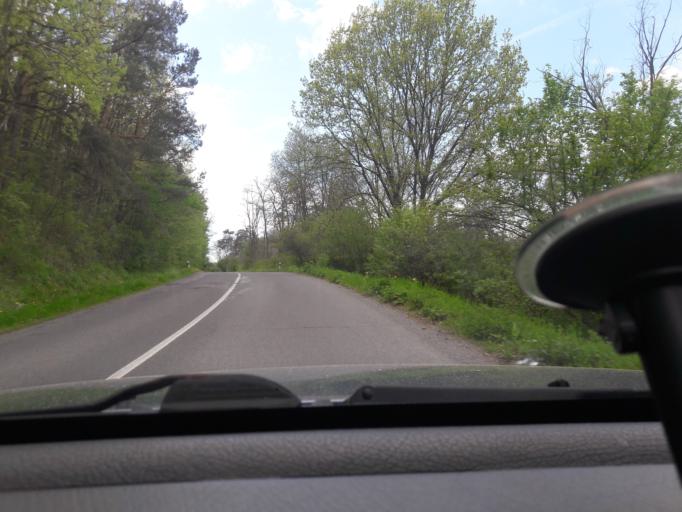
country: SK
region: Banskobystricky
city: Krupina
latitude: 48.3158
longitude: 19.0503
